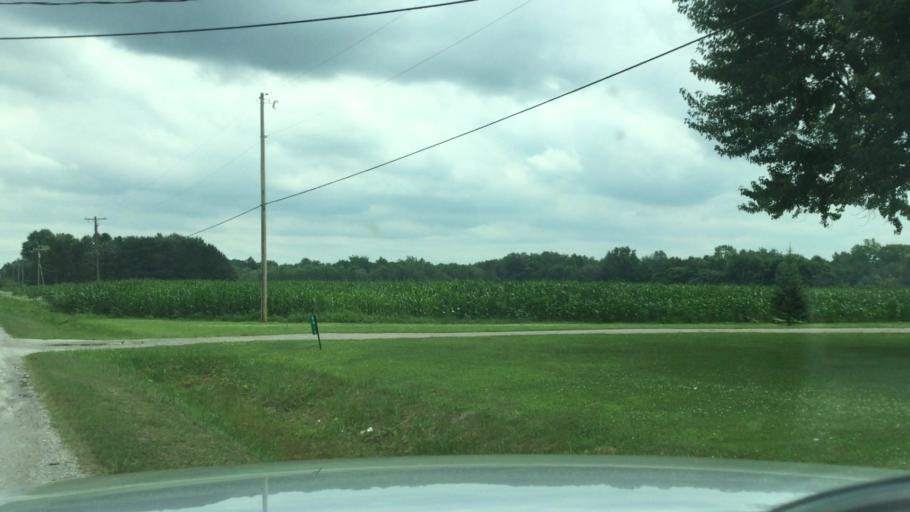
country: US
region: Michigan
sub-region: Saginaw County
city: Burt
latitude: 43.2948
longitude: -83.8938
